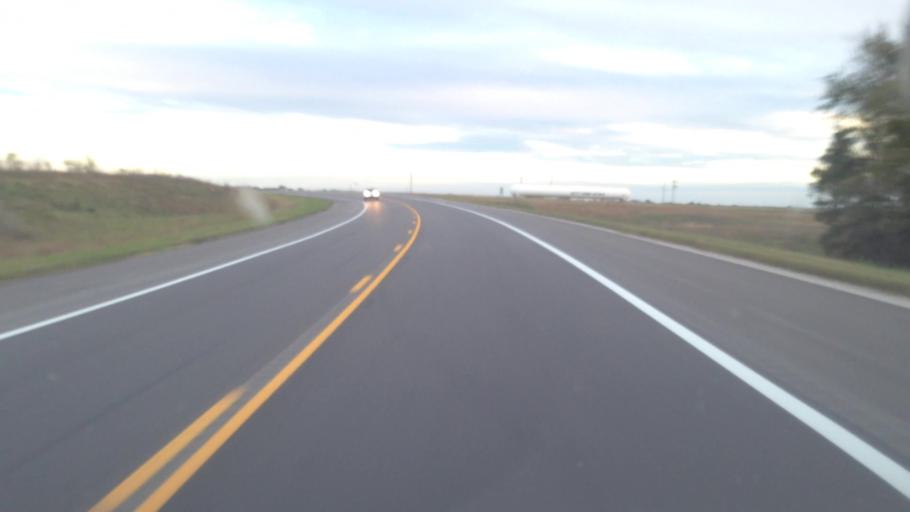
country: US
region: Kansas
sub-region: Franklin County
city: Ottawa
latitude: 38.4731
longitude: -95.2665
